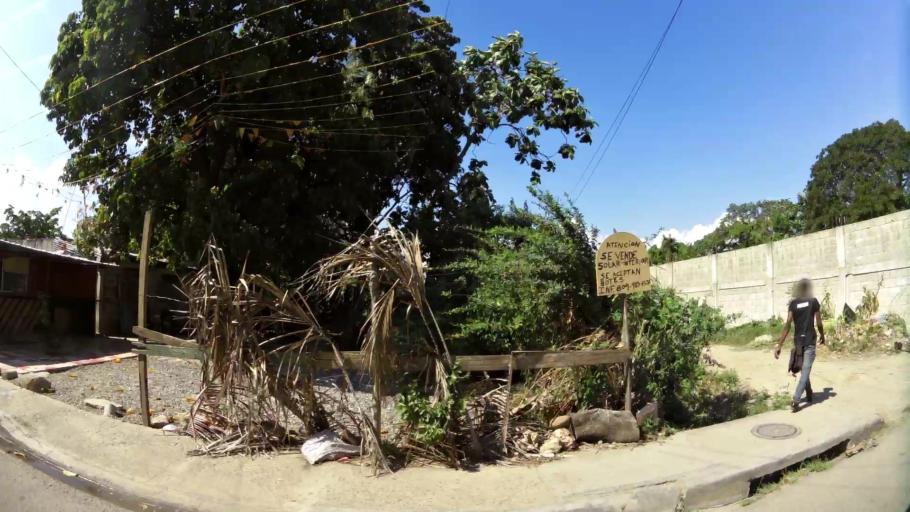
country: DO
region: Santo Domingo
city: Santo Domingo Oeste
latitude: 18.4719
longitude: -70.0014
